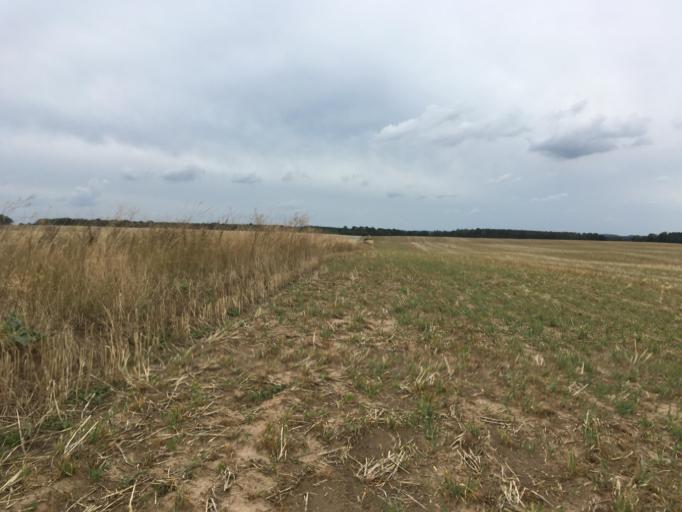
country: DE
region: Brandenburg
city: Passow
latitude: 53.1235
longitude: 14.1082
